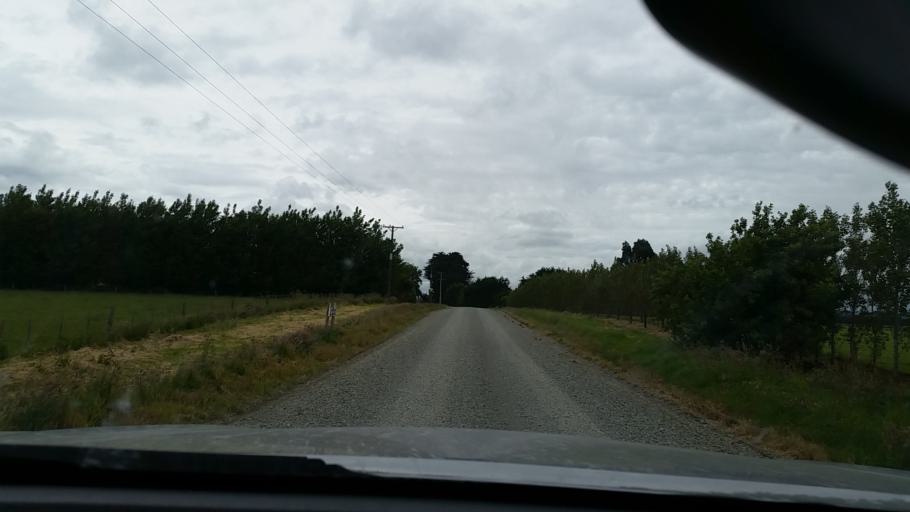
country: NZ
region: Southland
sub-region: Southland District
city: Winton
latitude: -46.1890
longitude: 168.2327
